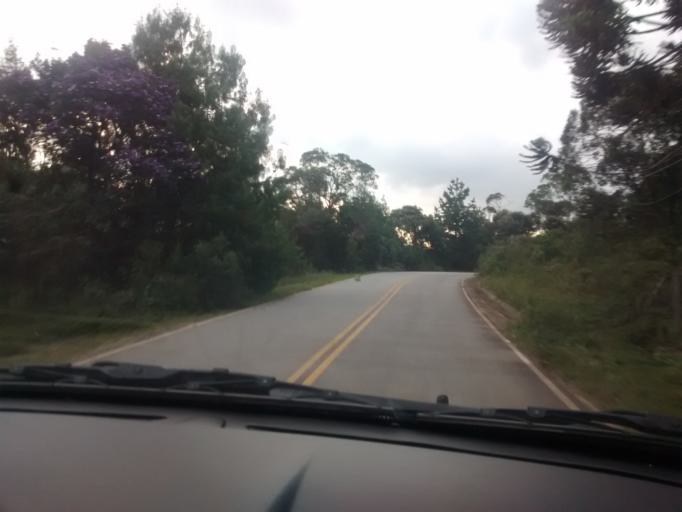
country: BR
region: Sao Paulo
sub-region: Campos Do Jordao
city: Campos do Jordao
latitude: -22.6610
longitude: -45.6258
